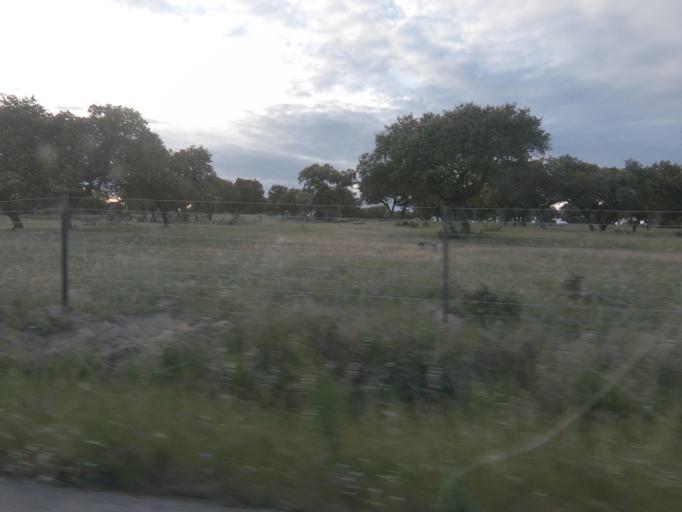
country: ES
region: Extremadura
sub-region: Provincia de Caceres
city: Malpartida de Caceres
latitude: 39.3936
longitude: -6.4274
